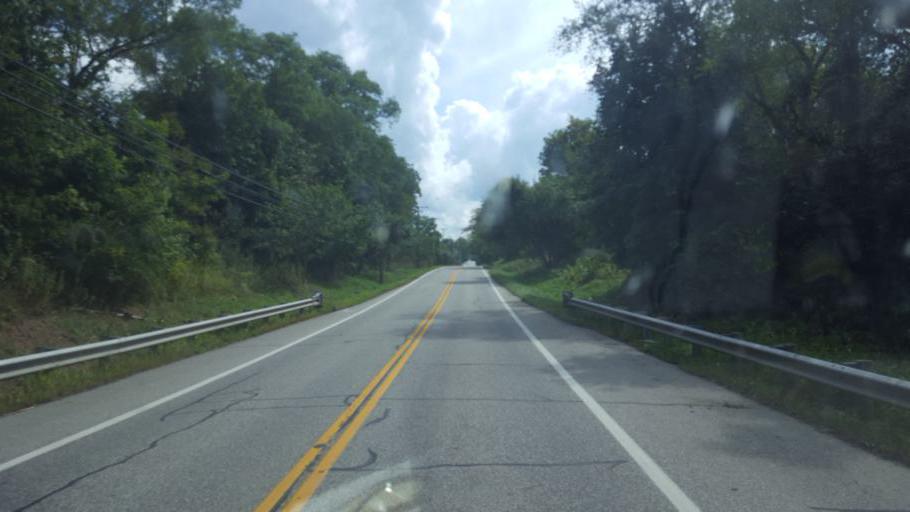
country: US
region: Ohio
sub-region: Geauga County
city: Burton
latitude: 41.3947
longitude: -81.1440
